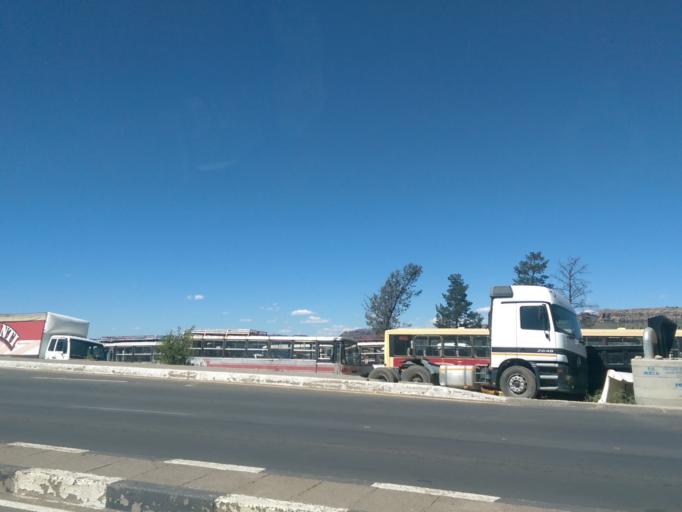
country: LS
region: Maseru
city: Maseru
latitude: -29.3287
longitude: 27.5039
